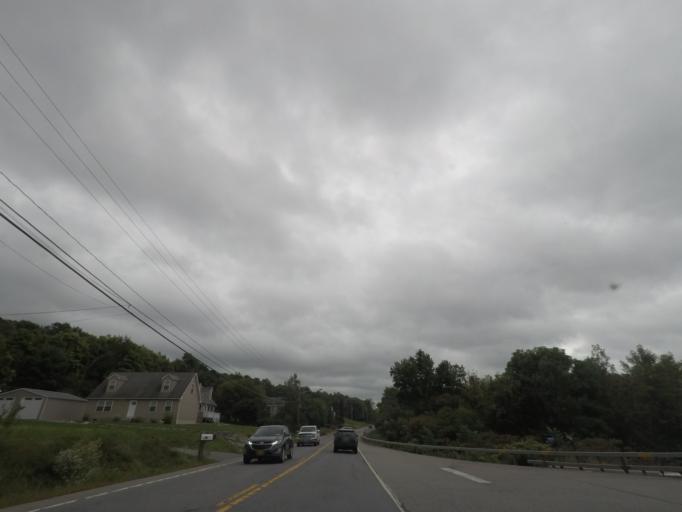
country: US
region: New York
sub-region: Saratoga County
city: Mechanicville
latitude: 42.9148
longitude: -73.7054
